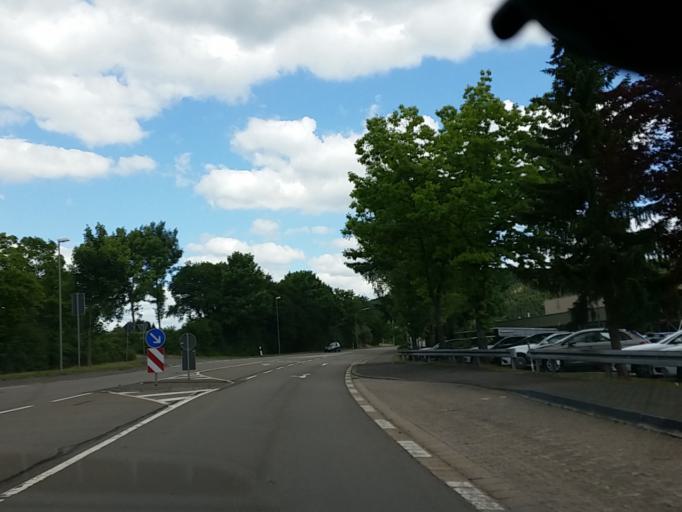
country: DE
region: Saarland
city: Wadern
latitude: 49.5267
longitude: 6.9060
